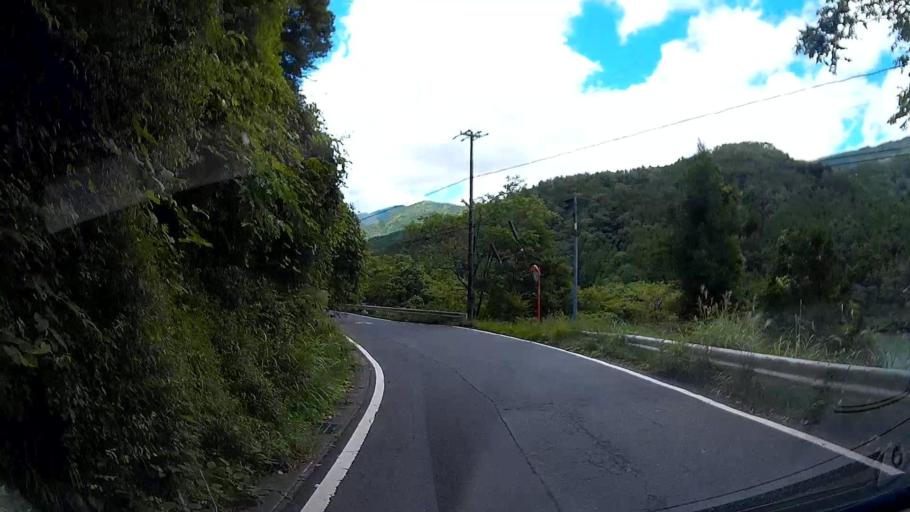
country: JP
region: Shizuoka
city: Shizuoka-shi
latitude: 35.2370
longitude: 138.2509
